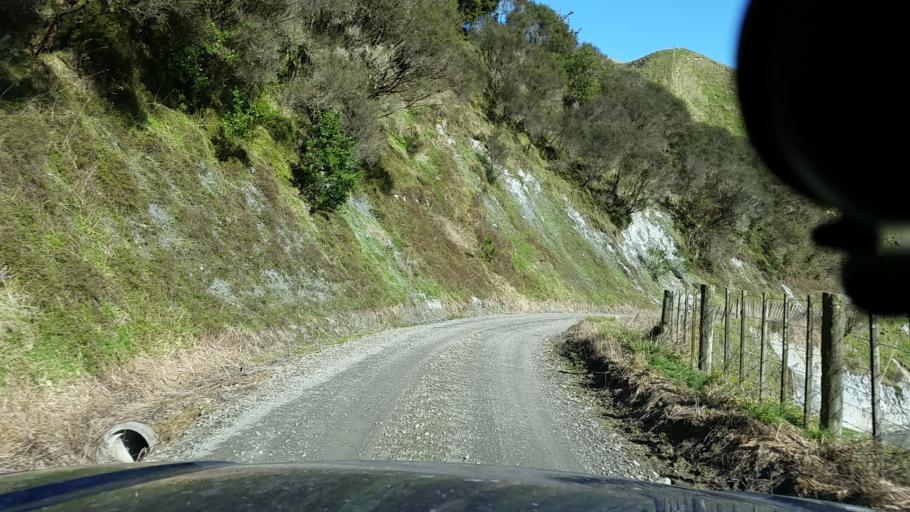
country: NZ
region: Taranaki
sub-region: New Plymouth District
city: Waitara
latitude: -39.0527
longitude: 174.7541
